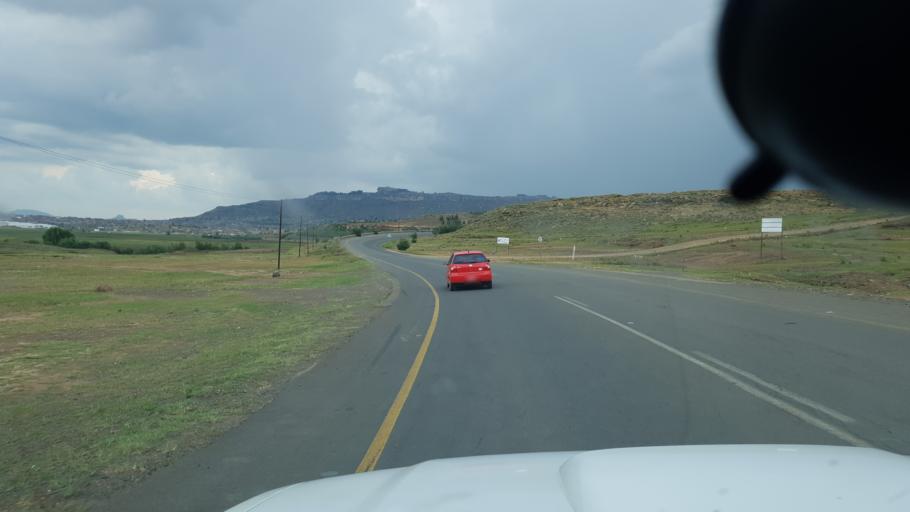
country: LS
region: Maseru
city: Maseru
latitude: -29.3877
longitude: 27.5048
